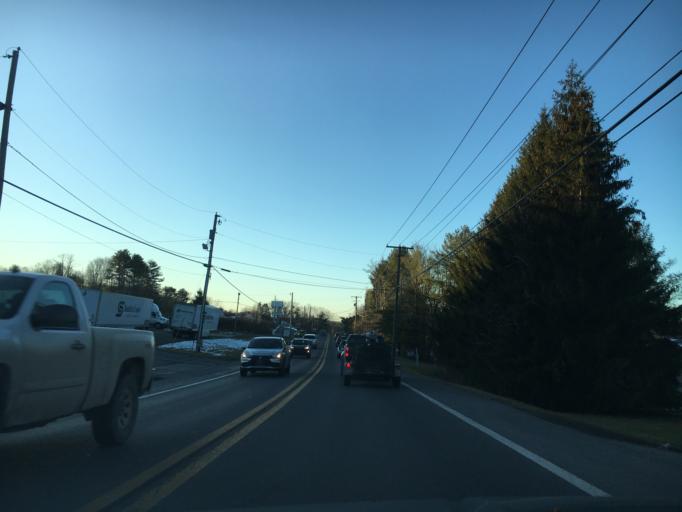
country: US
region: West Virginia
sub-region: Raleigh County
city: Daniels
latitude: 37.7409
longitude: -81.1171
